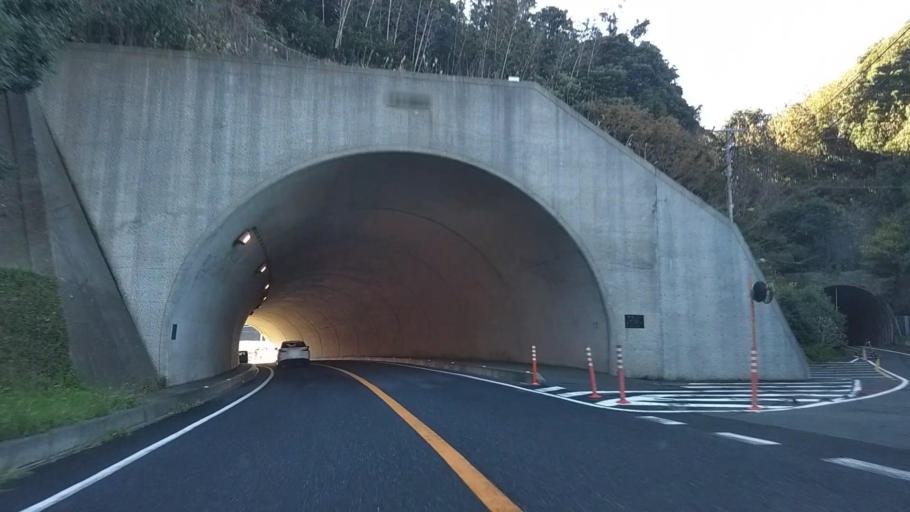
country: JP
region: Chiba
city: Futtsu
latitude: 35.1773
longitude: 139.8184
